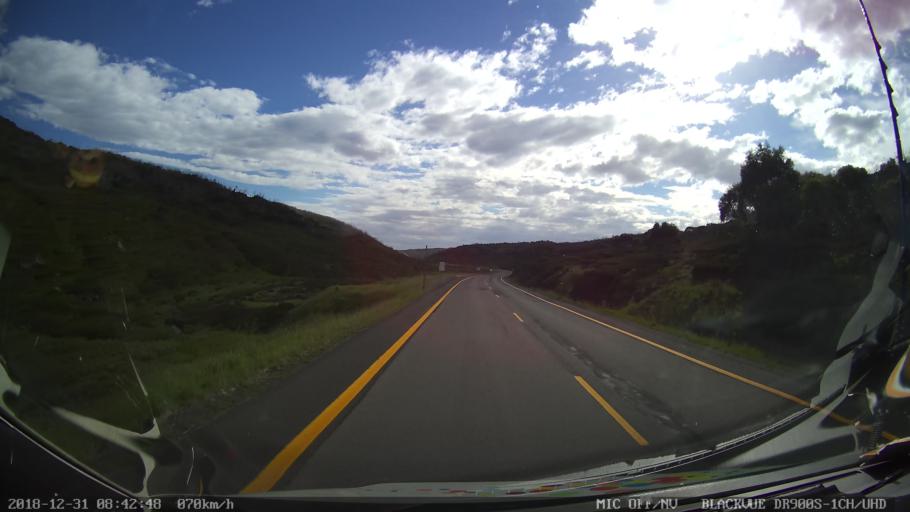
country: AU
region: New South Wales
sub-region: Snowy River
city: Jindabyne
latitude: -36.3924
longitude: 148.4371
